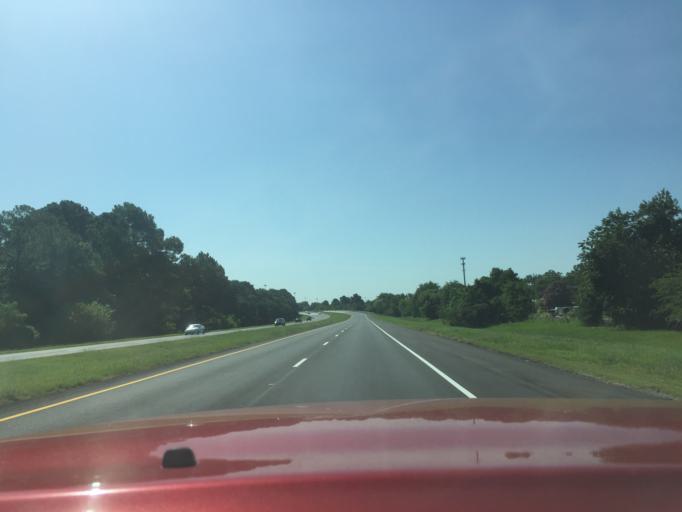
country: US
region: Georgia
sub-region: Chatham County
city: Garden City
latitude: 32.0954
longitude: -81.1364
